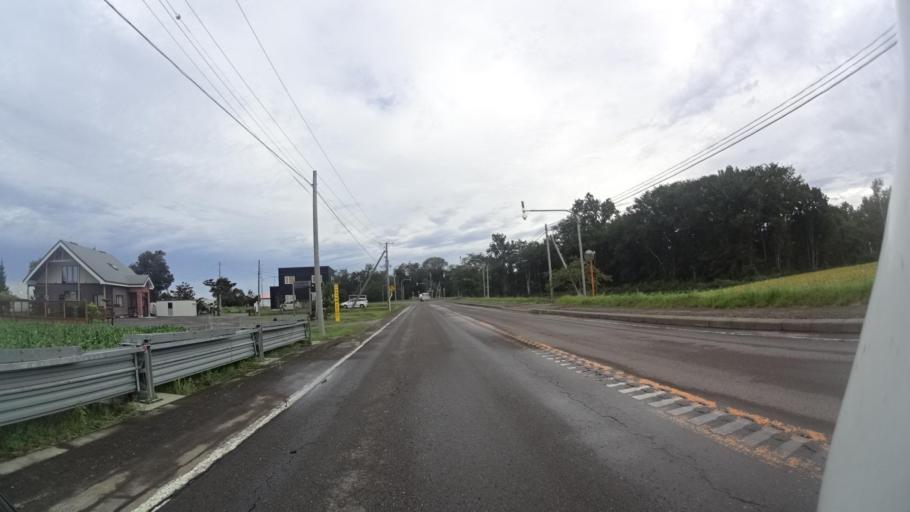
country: JP
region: Hokkaido
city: Abashiri
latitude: 43.8488
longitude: 144.5990
